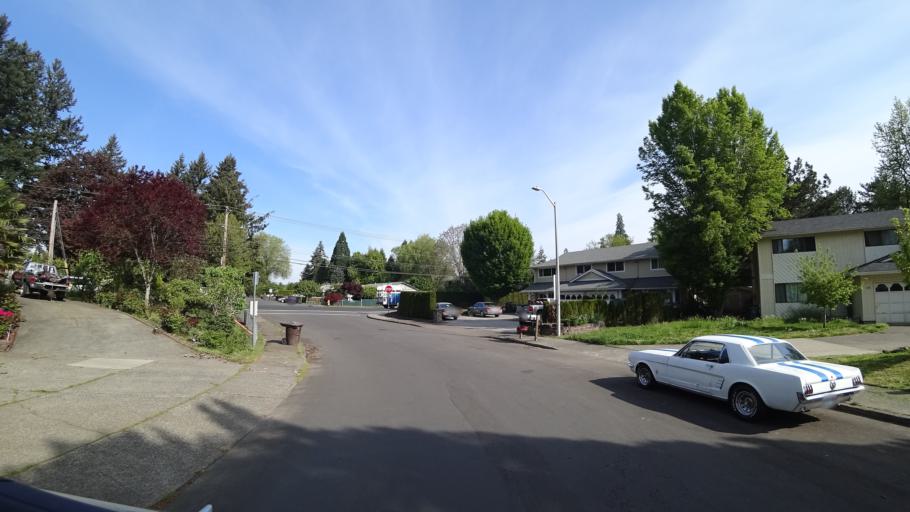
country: US
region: Oregon
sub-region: Washington County
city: Hillsboro
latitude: 45.5252
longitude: -122.9703
